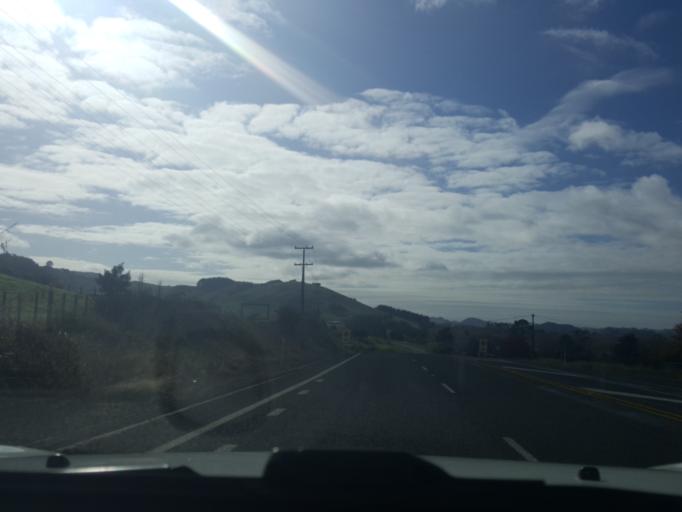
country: NZ
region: Waikato
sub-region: Hauraki District
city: Waihi
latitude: -37.4073
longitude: 175.8051
